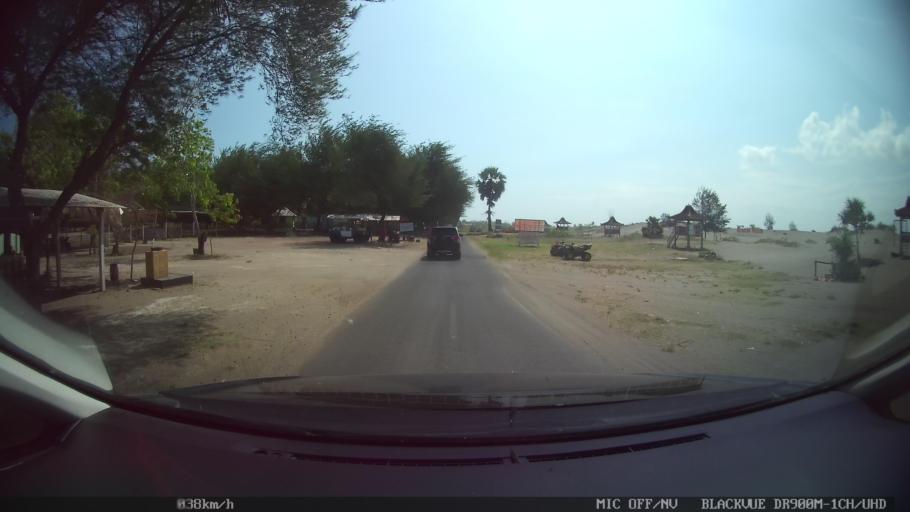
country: ID
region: Daerah Istimewa Yogyakarta
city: Pundong
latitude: -8.0183
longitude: 110.3169
